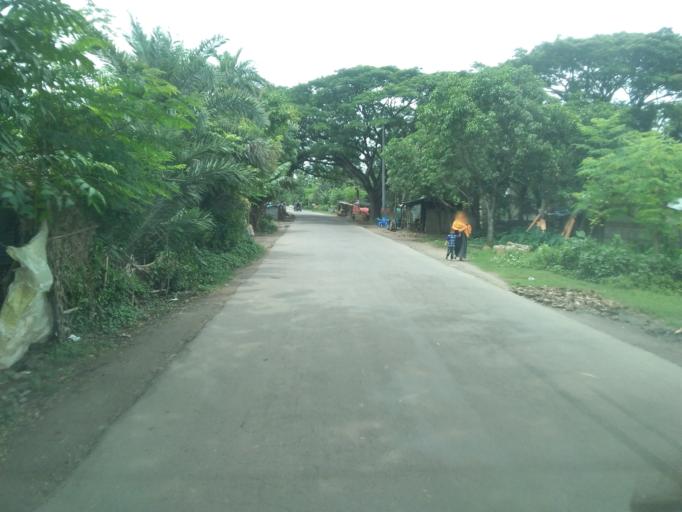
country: IN
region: West Bengal
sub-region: North 24 Parganas
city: Taki
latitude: 22.5806
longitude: 88.9983
